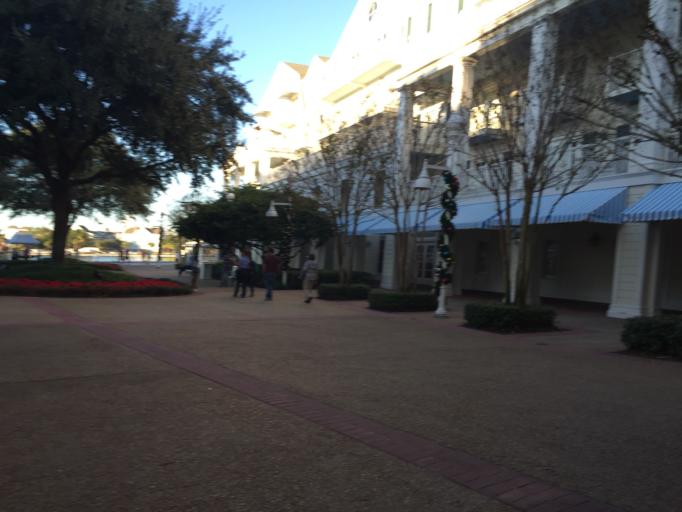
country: US
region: Florida
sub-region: Osceola County
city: Celebration
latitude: 28.3666
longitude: -81.5559
